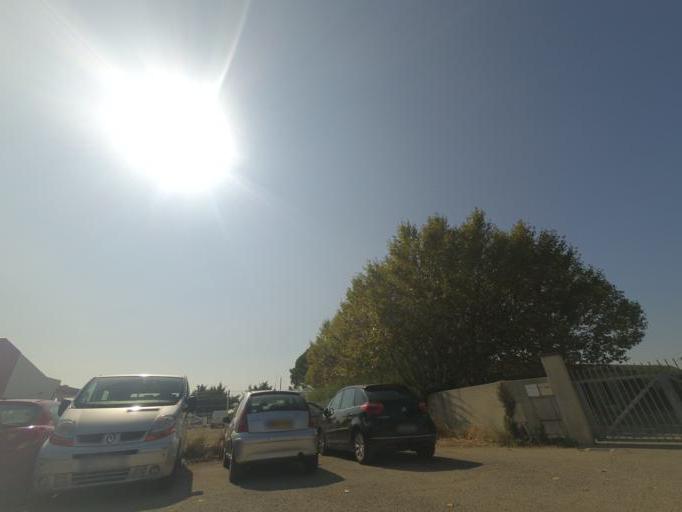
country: FR
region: Languedoc-Roussillon
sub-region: Departement du Gard
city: Calvisson
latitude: 43.7819
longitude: 4.2005
